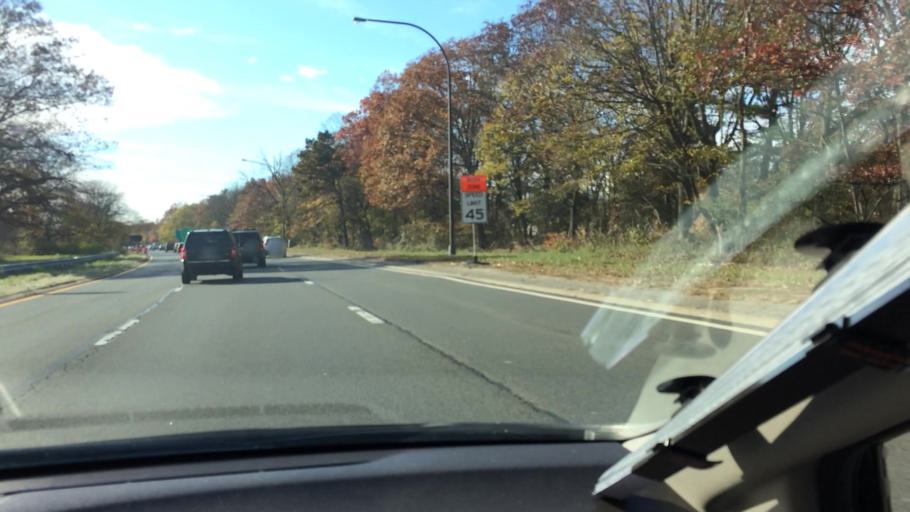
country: US
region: New York
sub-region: Suffolk County
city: West Babylon
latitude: 40.7325
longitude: -73.3586
